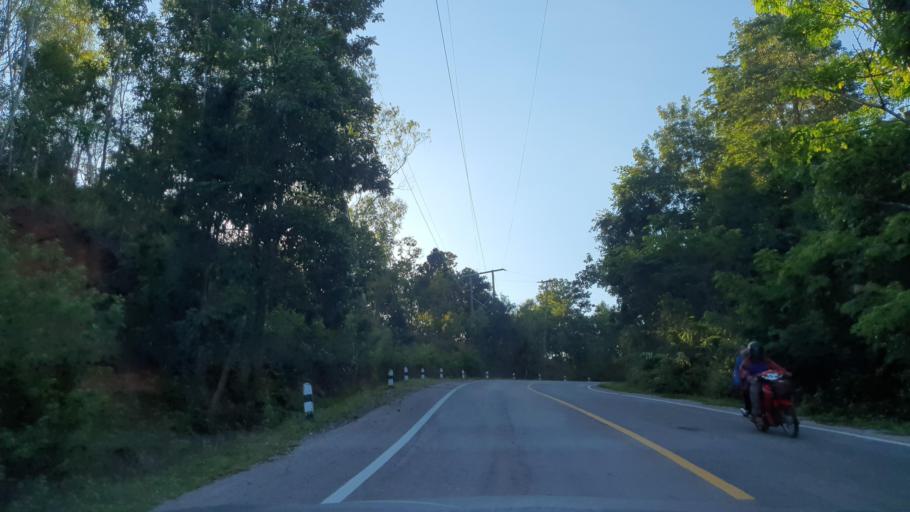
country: TH
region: Chiang Mai
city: Mae On
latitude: 18.8211
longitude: 99.3007
